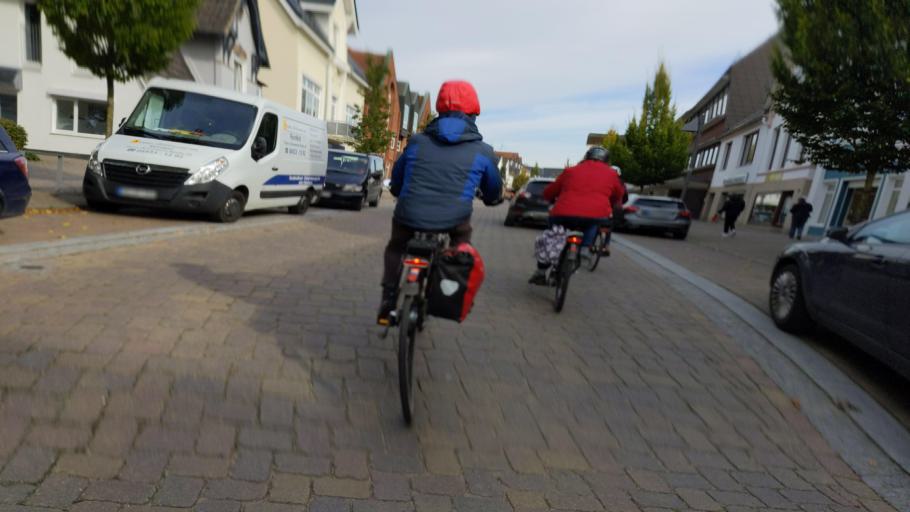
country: DE
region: Schleswig-Holstein
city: Reinfeld
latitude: 53.8311
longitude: 10.4880
